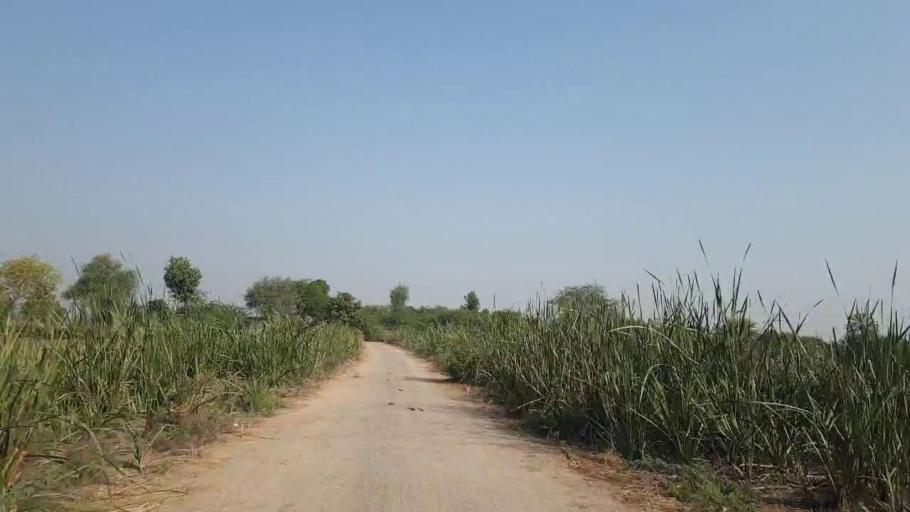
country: PK
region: Sindh
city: Matli
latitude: 25.0036
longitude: 68.6222
